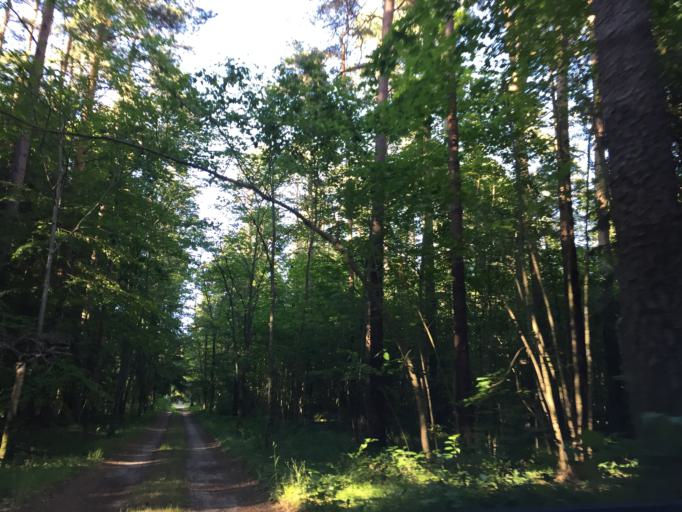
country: LV
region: Ventspils Rajons
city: Piltene
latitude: 57.3949
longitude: 21.8600
